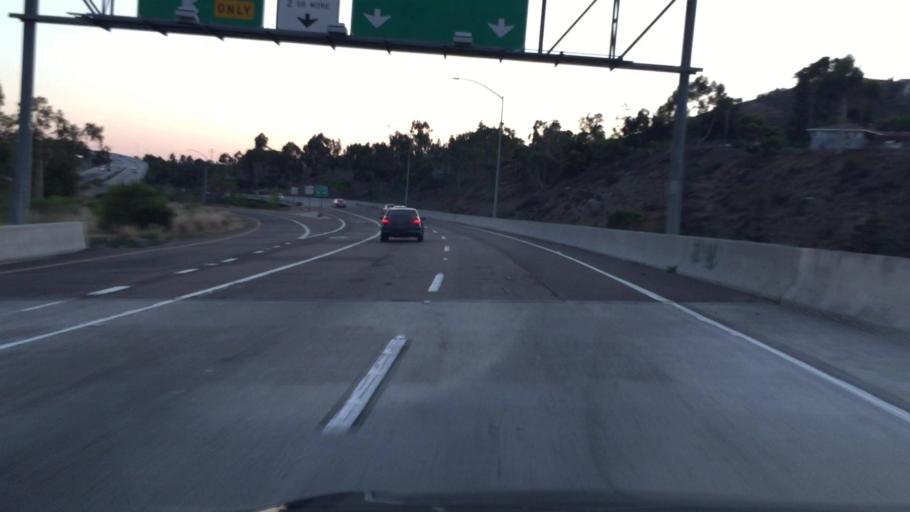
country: US
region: California
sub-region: San Diego County
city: Spring Valley
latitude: 32.7535
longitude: -117.0124
